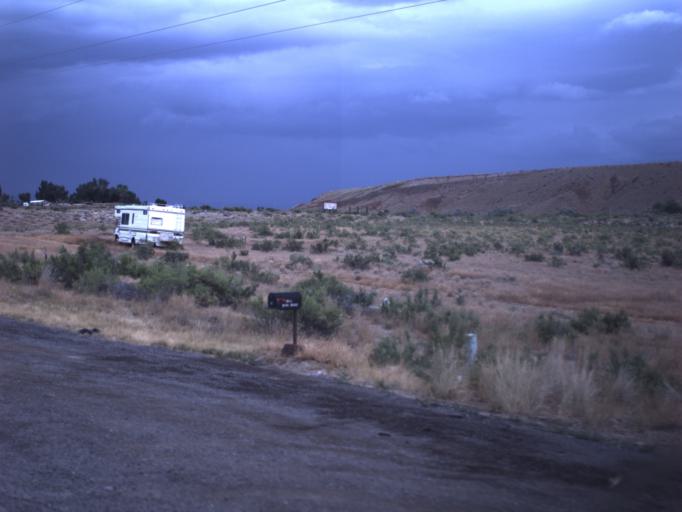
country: US
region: Utah
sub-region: Duchesne County
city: Roosevelt
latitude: 40.3420
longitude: -110.0256
